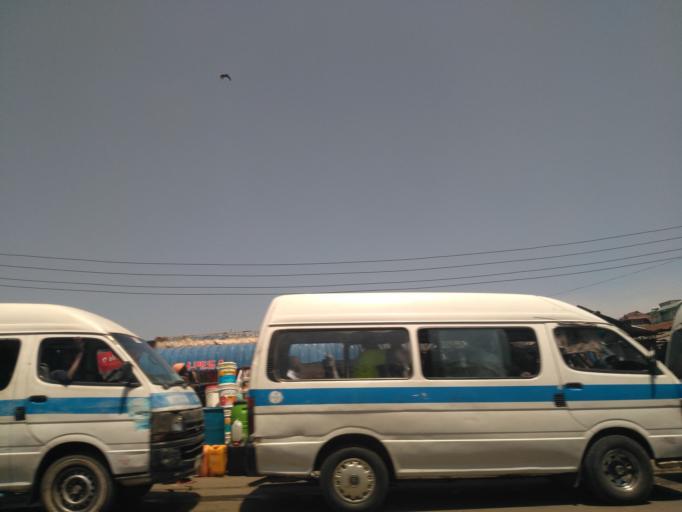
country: TZ
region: Mwanza
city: Mwanza
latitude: -2.5215
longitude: 32.9045
